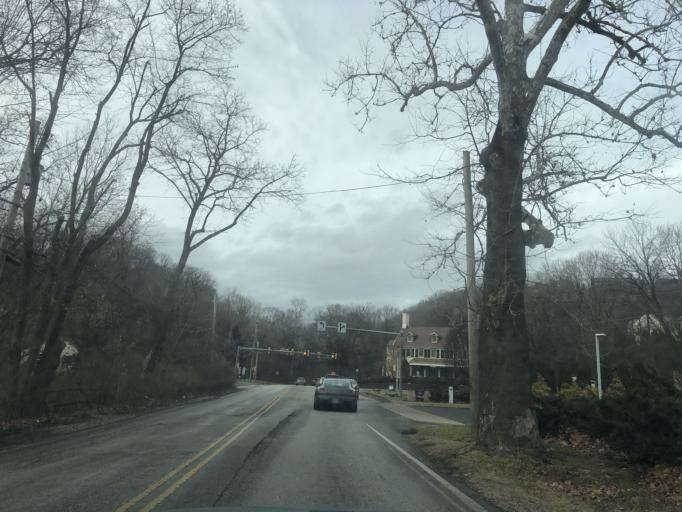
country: US
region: Pennsylvania
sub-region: Delaware County
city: Radnor
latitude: 40.0608
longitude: -75.3404
